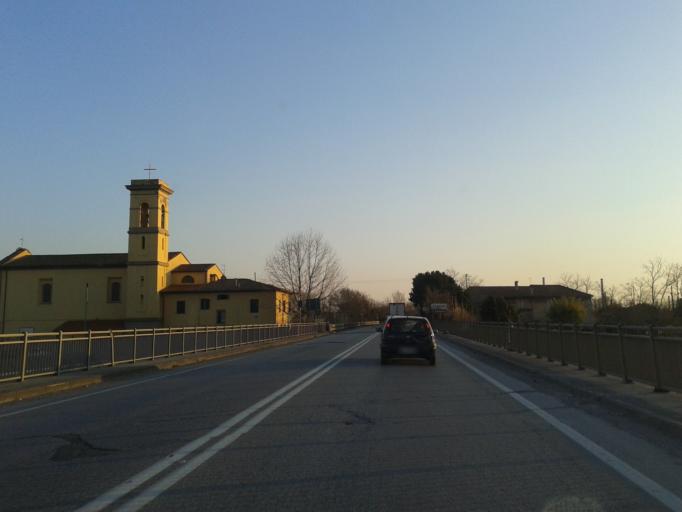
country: IT
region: Tuscany
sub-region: Provincia di Livorno
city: Guasticce
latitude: 43.5998
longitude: 10.3522
